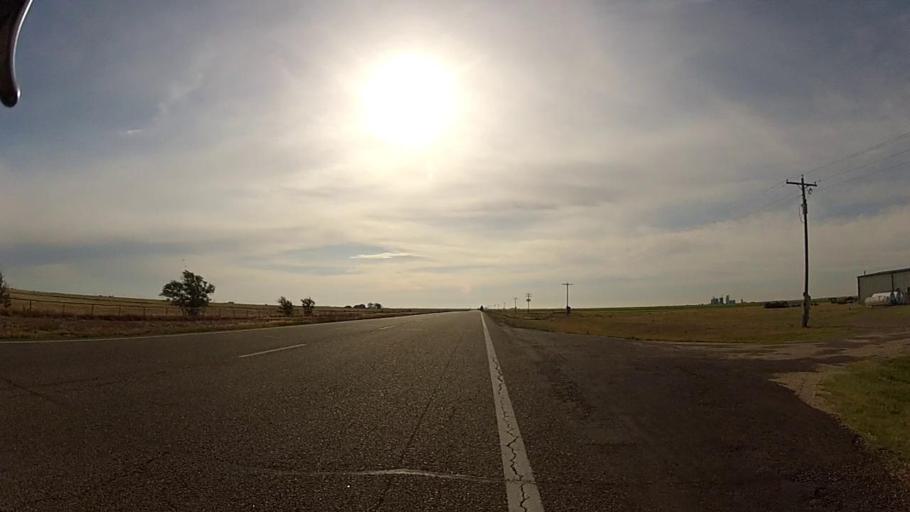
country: US
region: Kansas
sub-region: Grant County
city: Ulysses
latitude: 37.5766
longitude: -101.4829
